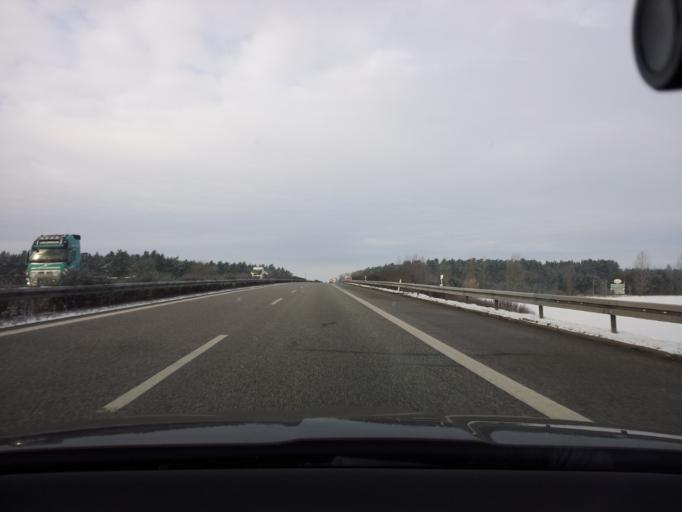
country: DE
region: Mecklenburg-Vorpommern
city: Sulstorf
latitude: 53.4764
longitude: 11.2994
